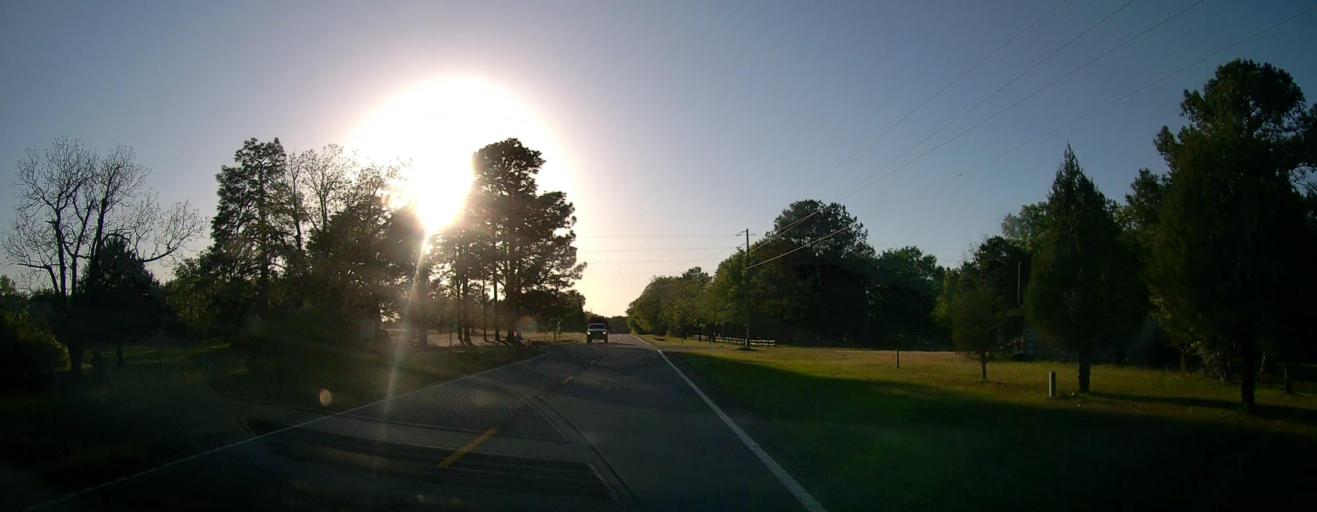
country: US
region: Georgia
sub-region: Schley County
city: Ellaville
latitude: 32.3313
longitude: -84.3415
